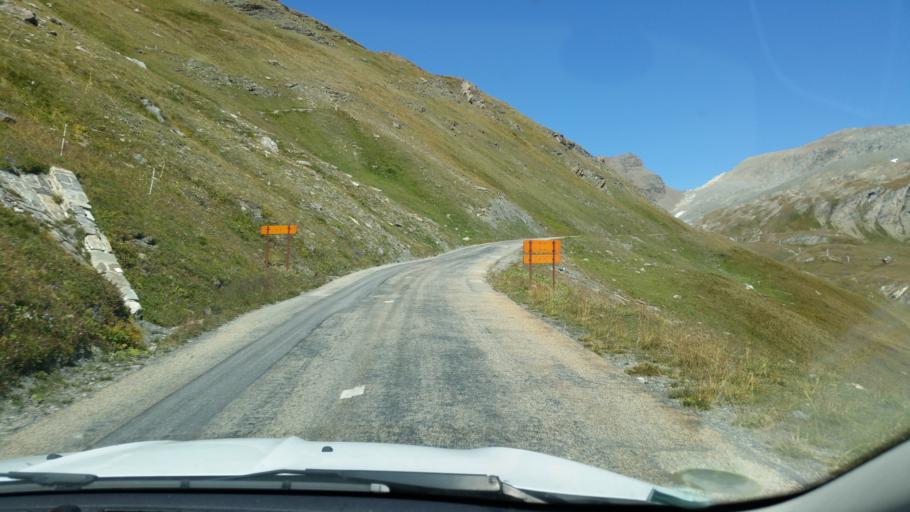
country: FR
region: Rhone-Alpes
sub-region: Departement de la Savoie
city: Val-d'Isere
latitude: 45.4122
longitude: 7.0296
